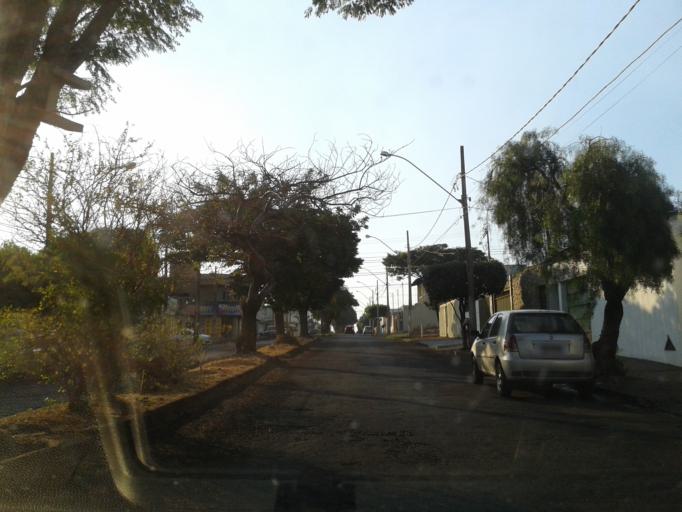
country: BR
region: Minas Gerais
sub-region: Uberlandia
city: Uberlandia
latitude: -18.9030
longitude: -48.2448
